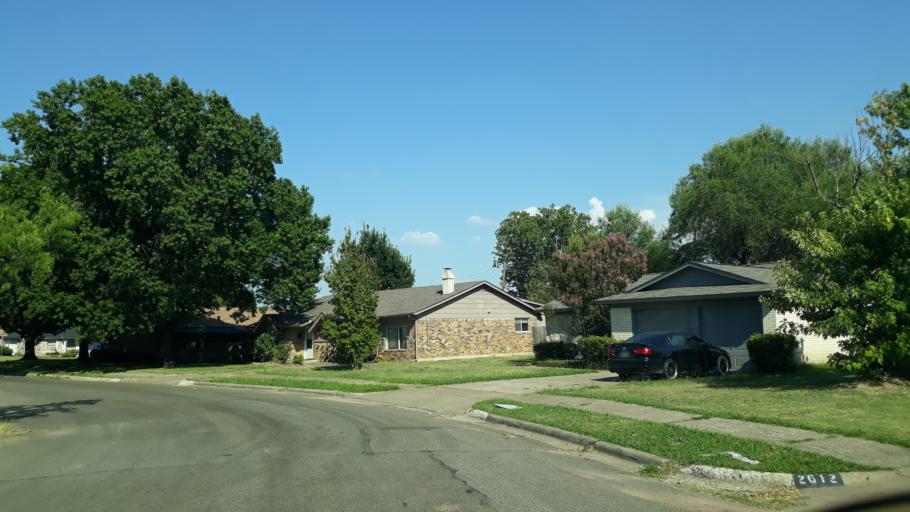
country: US
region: Texas
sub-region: Dallas County
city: Irving
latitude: 32.8439
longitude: -97.0050
